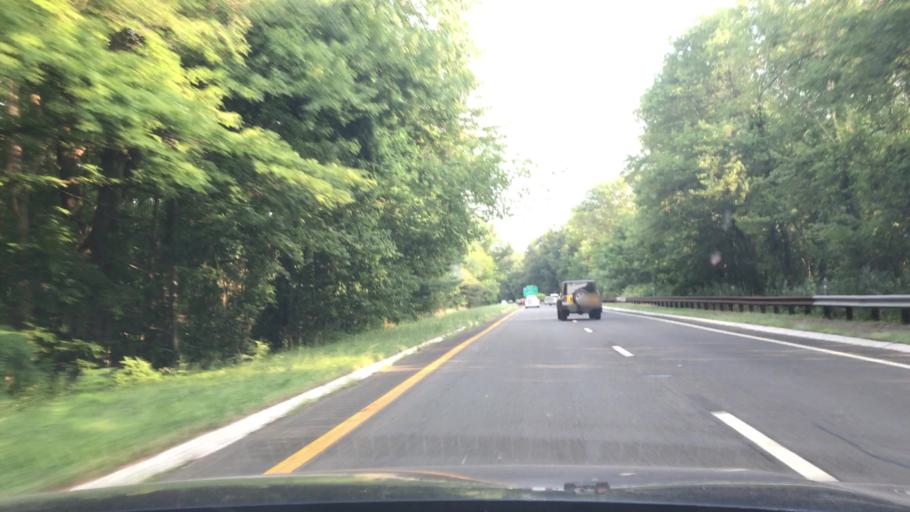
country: US
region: New York
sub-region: Rockland County
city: Bardonia
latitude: 41.1149
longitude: -74.0028
